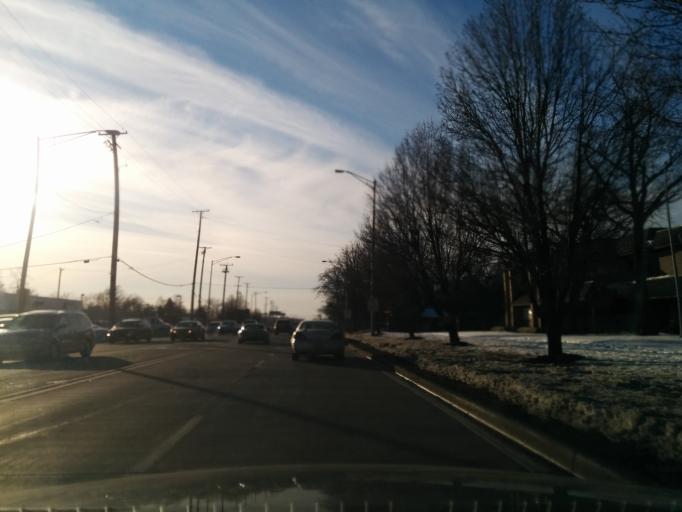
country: US
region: Illinois
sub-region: DuPage County
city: Elmhurst
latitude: 41.9059
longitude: -87.9592
